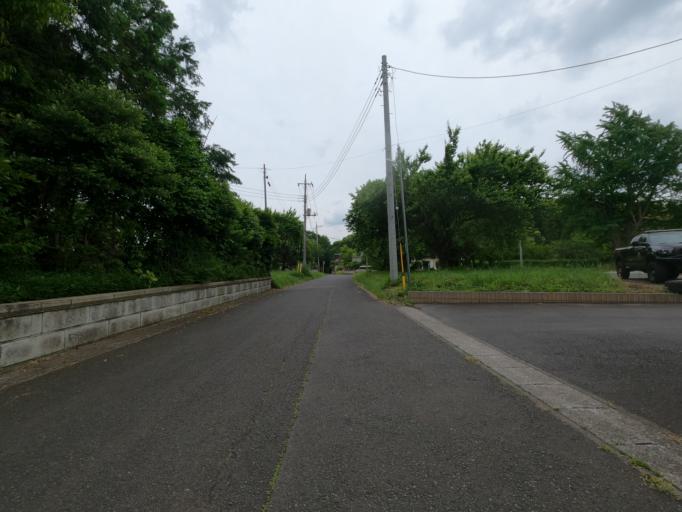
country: JP
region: Ibaraki
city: Moriya
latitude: 35.9532
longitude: 139.9682
